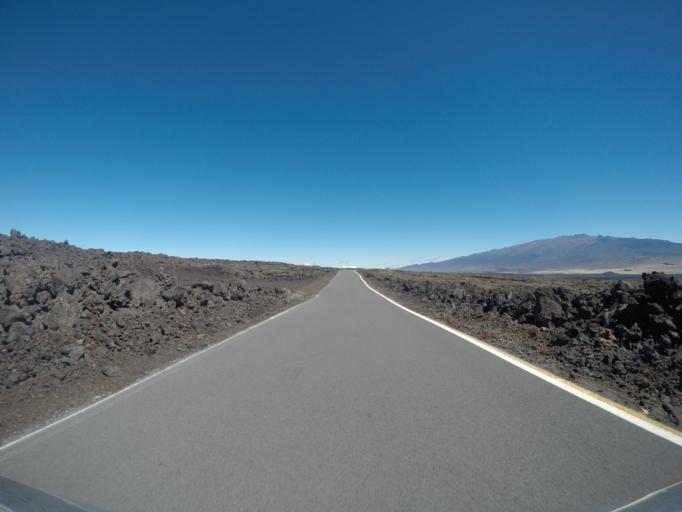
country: US
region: Hawaii
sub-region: Hawaii County
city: Volcano
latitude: 19.6207
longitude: -155.4735
